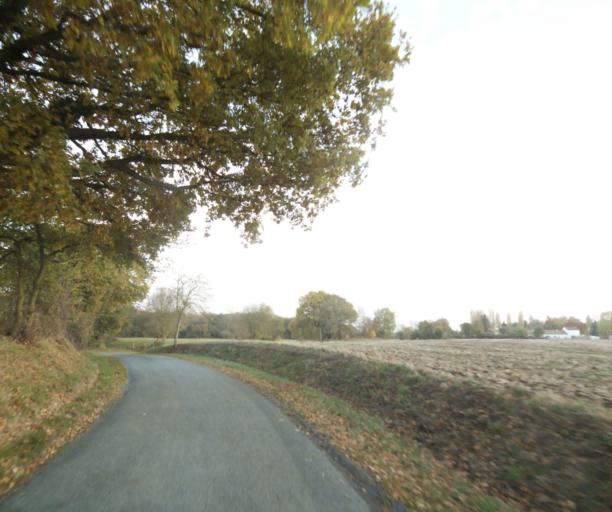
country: FR
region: Poitou-Charentes
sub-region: Departement de la Charente-Maritime
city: Saintes
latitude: 45.7641
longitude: -0.6484
